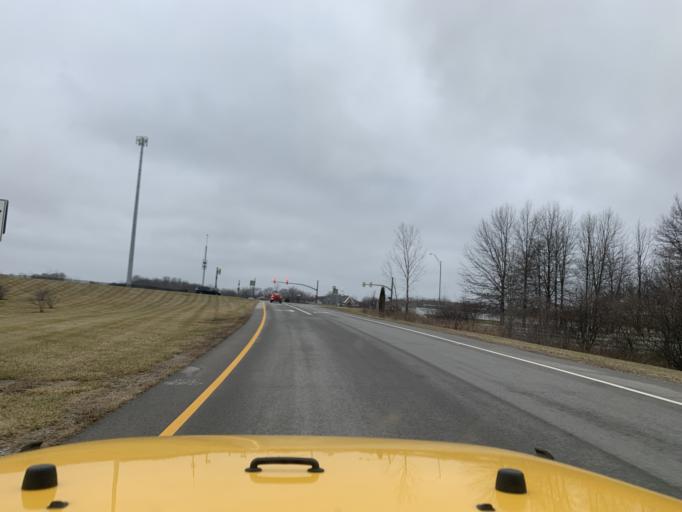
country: US
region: Ohio
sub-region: Franklin County
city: New Albany
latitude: 40.0924
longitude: -82.8217
